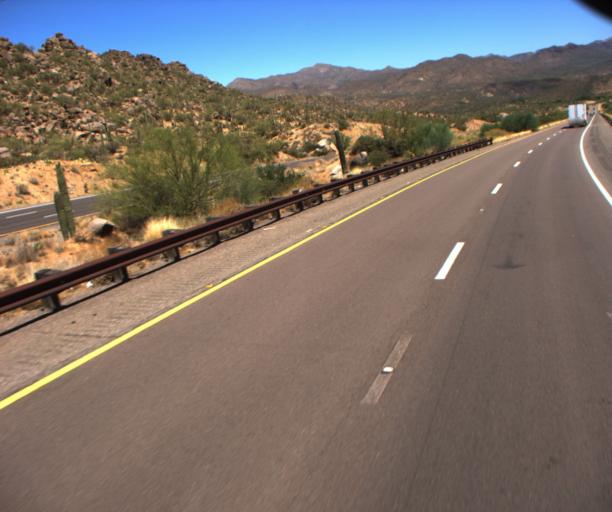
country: US
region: Arizona
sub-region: Maricopa County
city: Rio Verde
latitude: 33.7135
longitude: -111.5101
